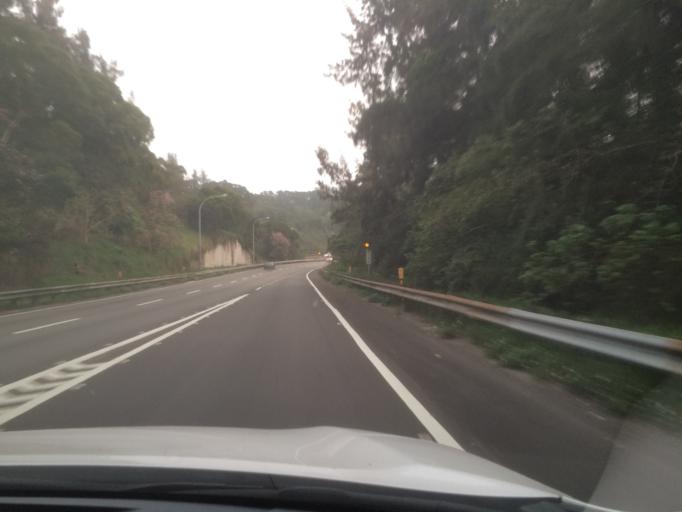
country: TW
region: Taiwan
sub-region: Hsinchu
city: Hsinchu
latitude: 24.7553
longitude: 120.9844
